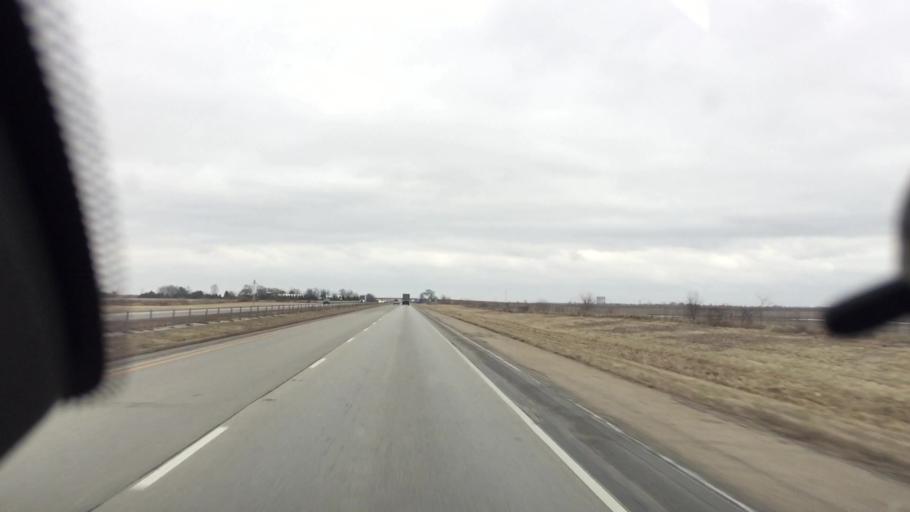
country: US
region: Illinois
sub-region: Vermilion County
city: Oakwood
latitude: 40.1245
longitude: -87.8247
